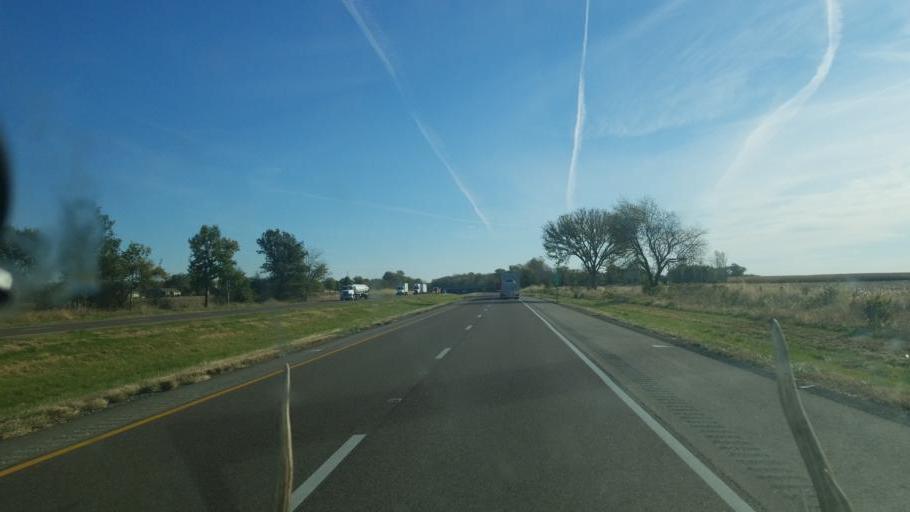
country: US
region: Illinois
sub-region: Madison County
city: Troy
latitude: 38.7556
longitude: -89.8549
